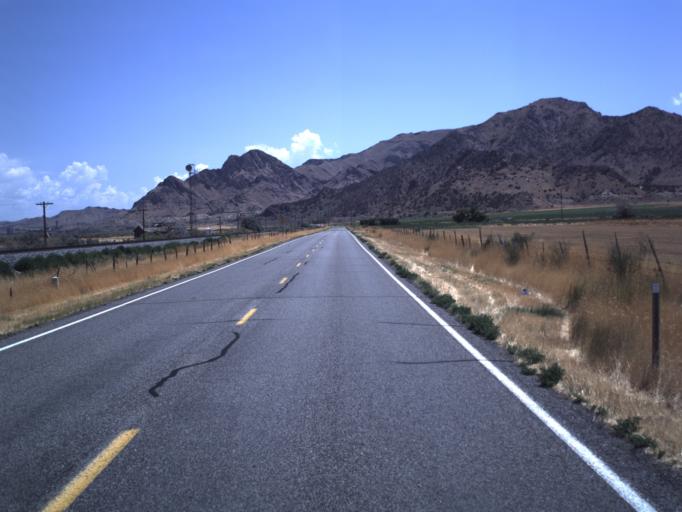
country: US
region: Utah
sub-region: Millard County
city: Delta
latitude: 39.5368
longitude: -112.2673
